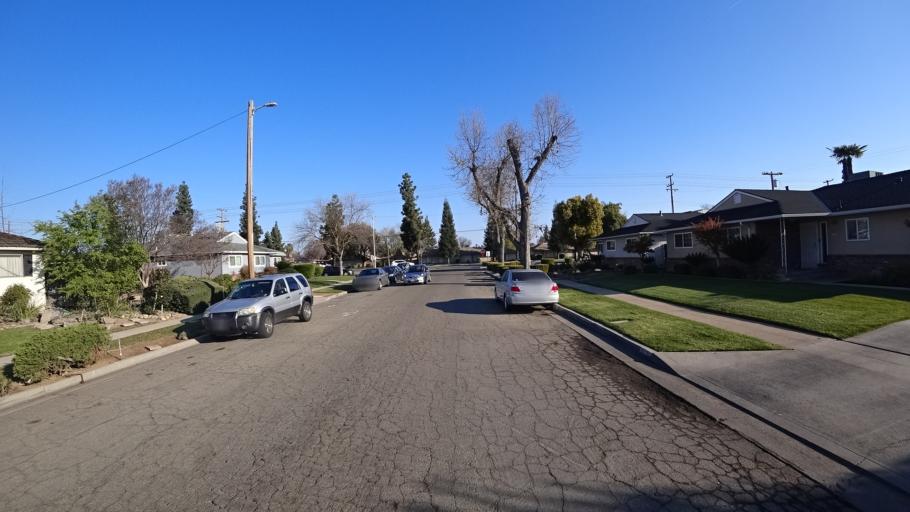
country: US
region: California
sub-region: Fresno County
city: Fresno
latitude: 36.8224
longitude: -119.7780
